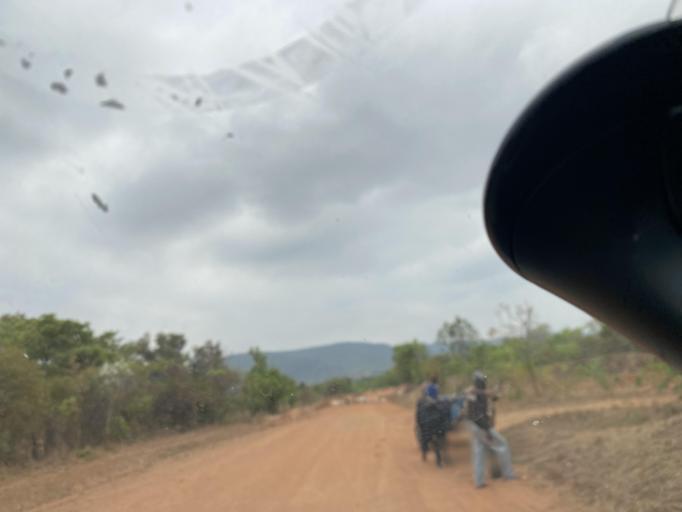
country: ZM
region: Lusaka
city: Chongwe
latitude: -15.2011
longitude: 28.7627
